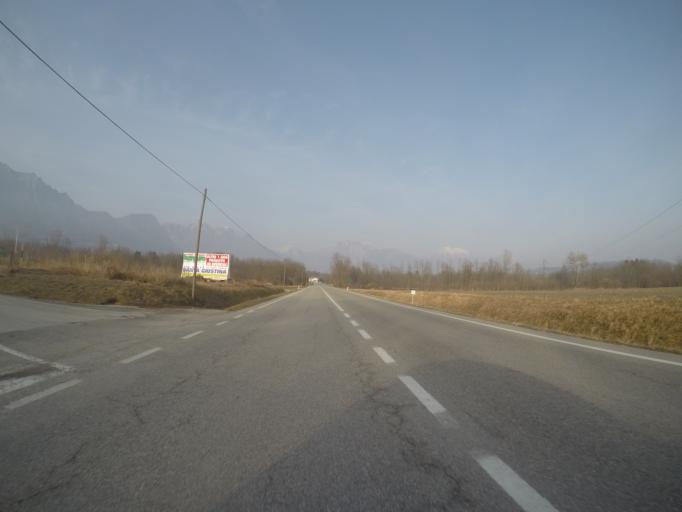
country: IT
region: Veneto
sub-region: Provincia di Belluno
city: Sedico
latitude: 46.1119
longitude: 12.0728
